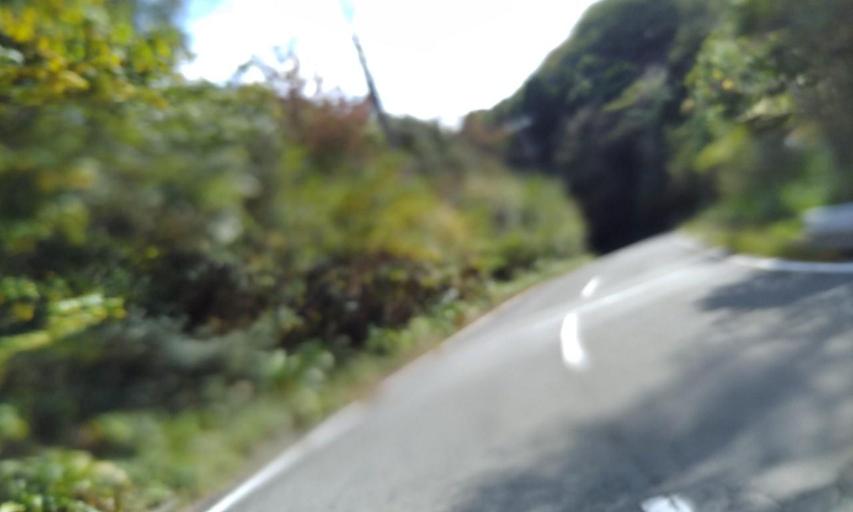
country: JP
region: Wakayama
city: Gobo
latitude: 33.9680
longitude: 135.0952
